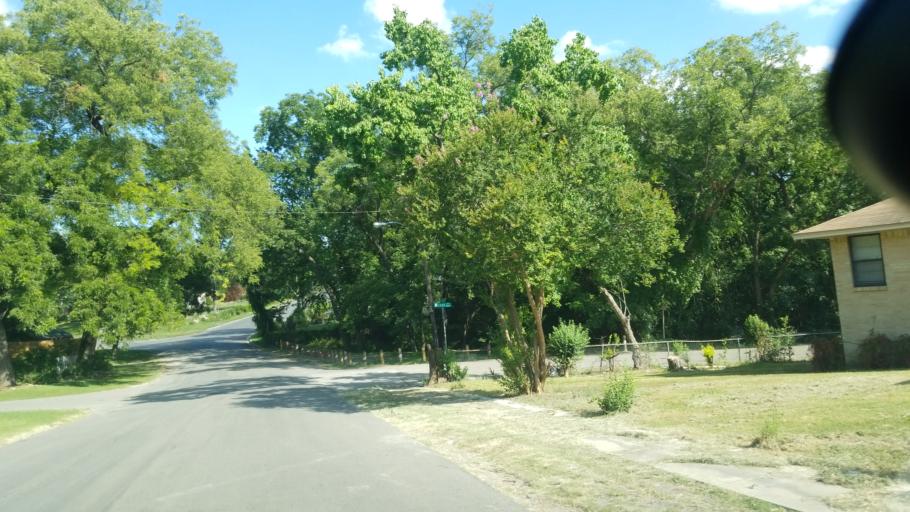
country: US
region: Texas
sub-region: Dallas County
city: Balch Springs
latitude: 32.7710
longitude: -96.7099
